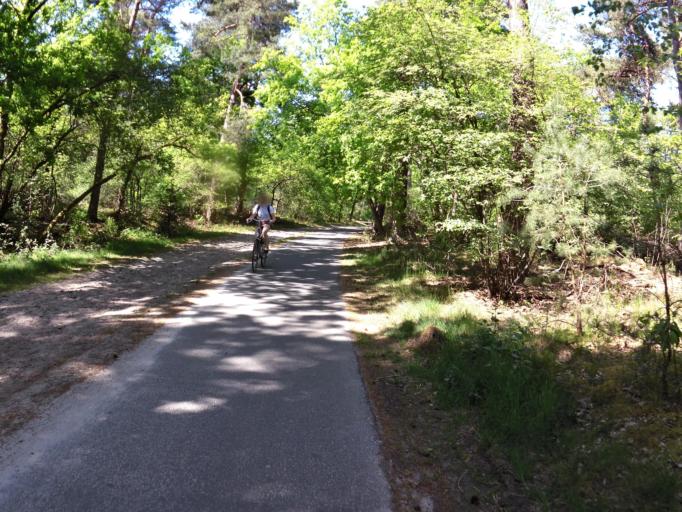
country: NL
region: North Brabant
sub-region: Gemeente Loon op Zand
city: Loon op Zand
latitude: 51.6437
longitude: 5.0728
